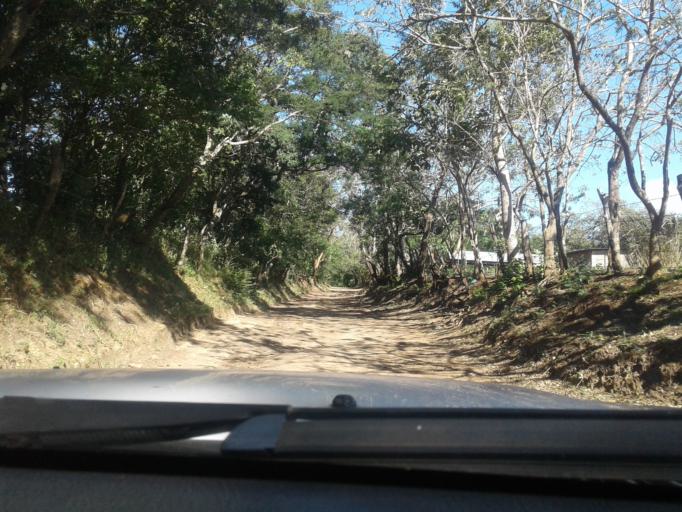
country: NI
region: Carazo
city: Santa Teresa
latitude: 11.7774
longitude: -86.1793
